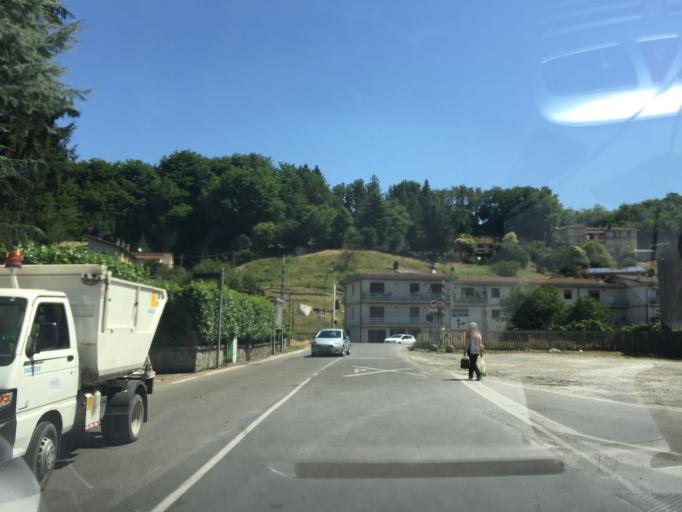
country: IT
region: Tuscany
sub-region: Provincia di Lucca
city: Castelnuovo di Garfagnana
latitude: 44.1191
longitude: 10.4063
